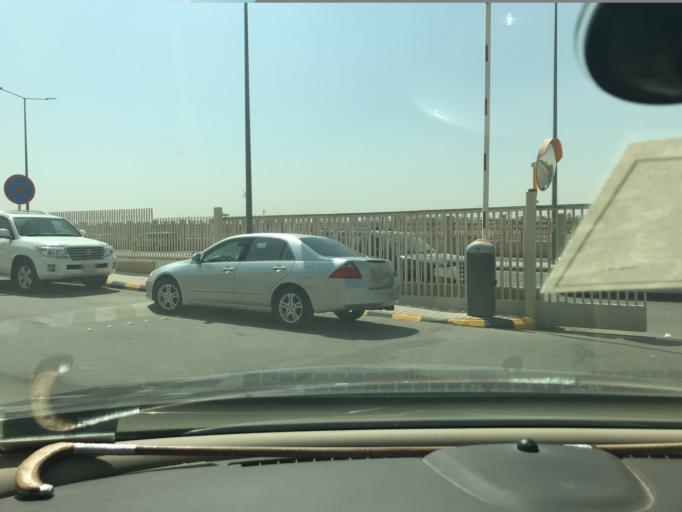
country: SA
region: Ar Riyad
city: Riyadh
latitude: 24.7082
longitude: 46.7925
